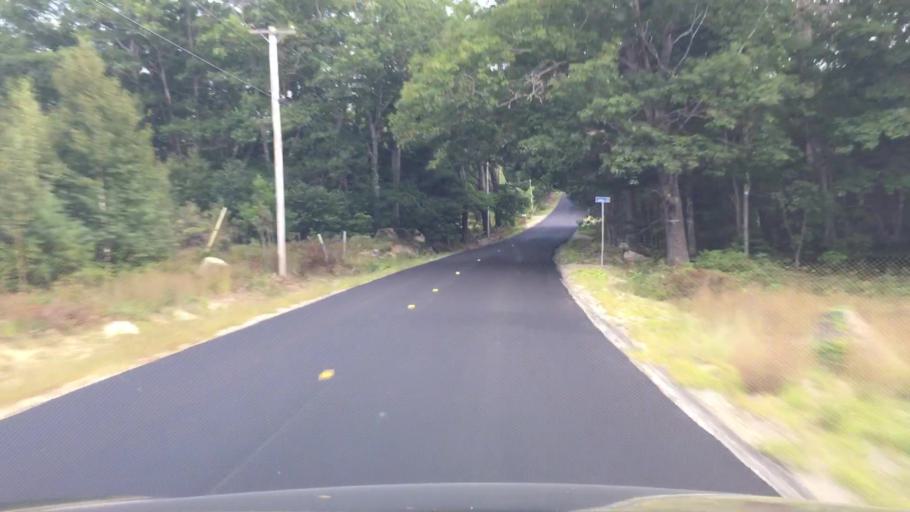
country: US
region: Maine
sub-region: Hancock County
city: Surry
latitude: 44.5257
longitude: -68.6096
